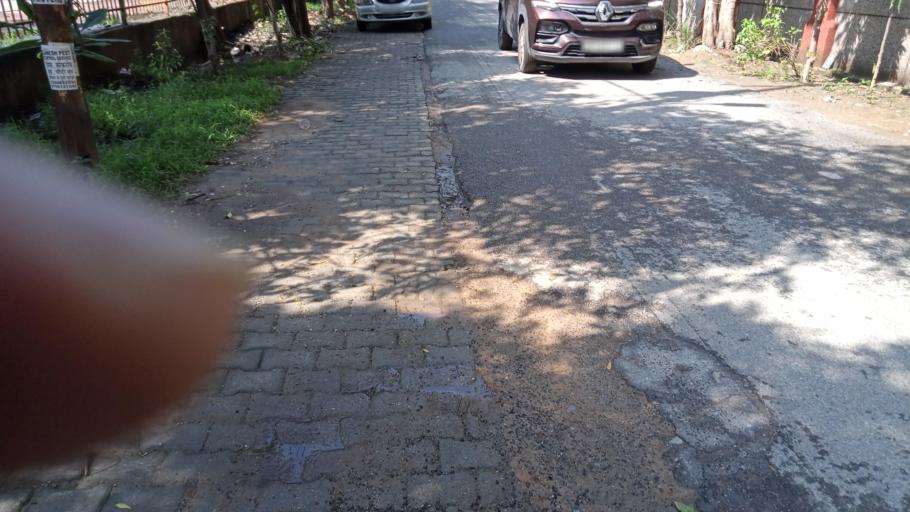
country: IN
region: Uttar Pradesh
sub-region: Ghaziabad
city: Ghaziabad
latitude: 28.6643
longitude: 77.3725
